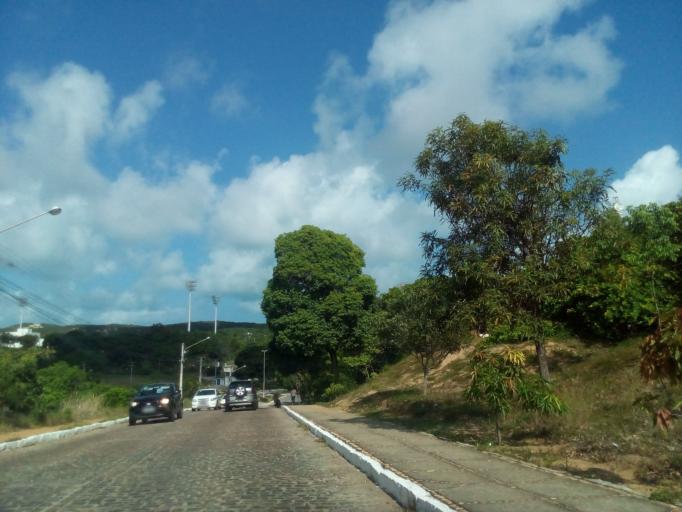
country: BR
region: Rio Grande do Norte
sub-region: Natal
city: Natal
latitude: -5.8375
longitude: -35.2046
